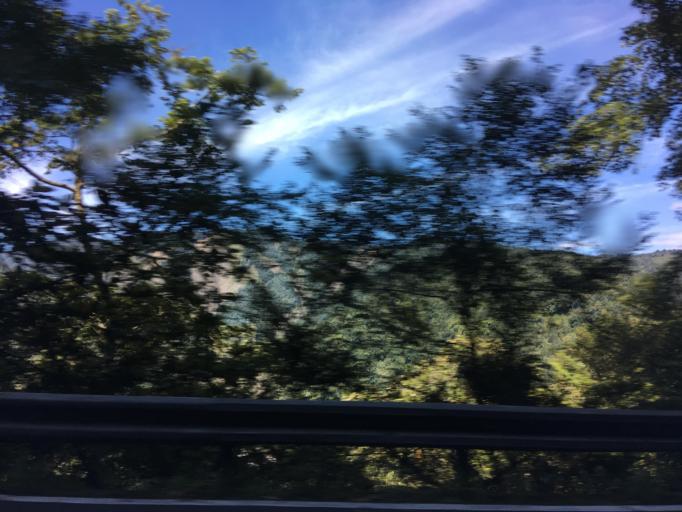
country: TW
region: Taiwan
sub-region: Yilan
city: Yilan
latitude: 24.5488
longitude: 121.5119
